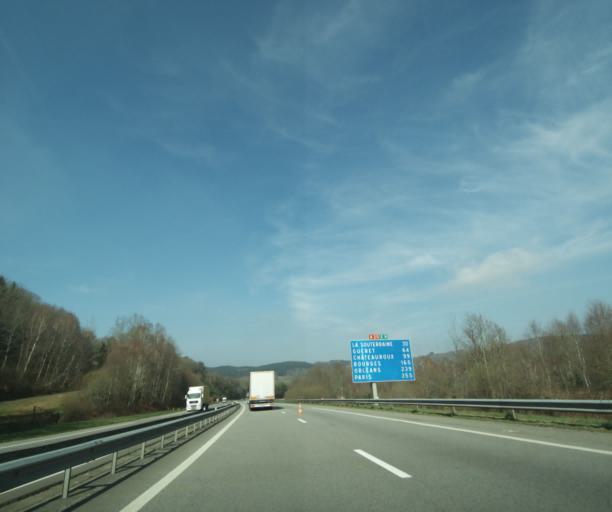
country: FR
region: Limousin
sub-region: Departement de la Haute-Vienne
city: Razes
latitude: 46.0343
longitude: 1.3497
